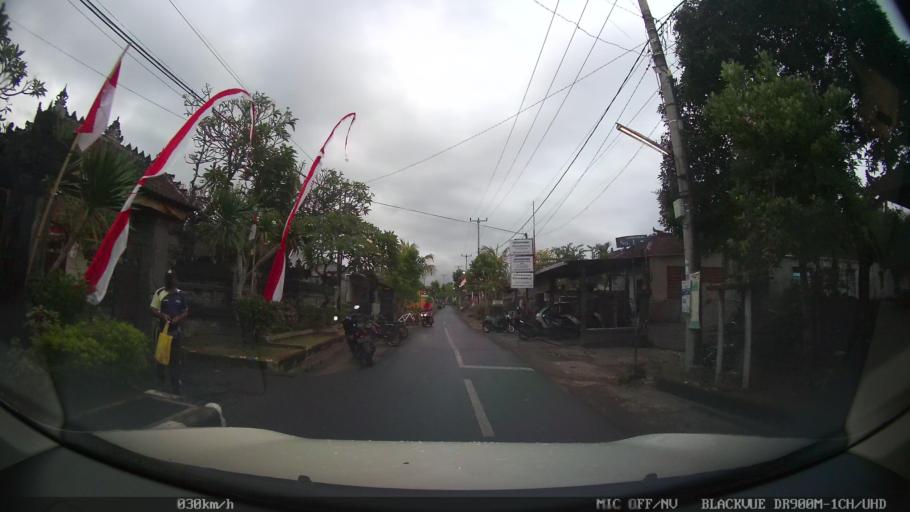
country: ID
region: Bali
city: Banjar Pasekan
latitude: -8.6216
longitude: 115.2743
